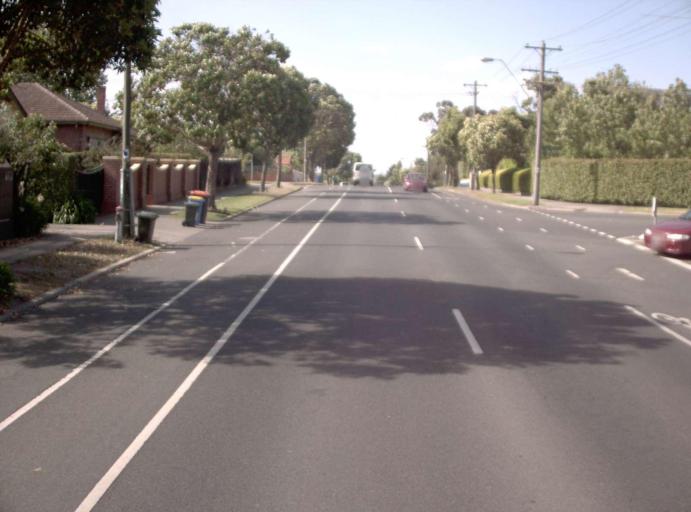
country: AU
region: Victoria
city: Glenferrie
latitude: -37.8363
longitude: 145.0466
